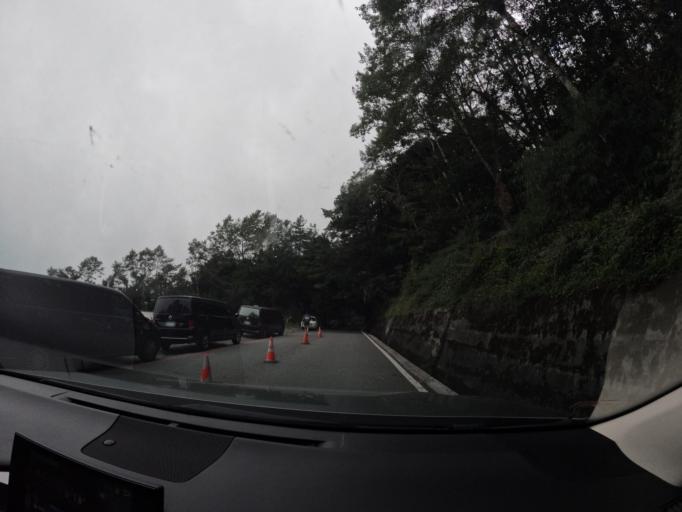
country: TW
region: Taiwan
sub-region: Taitung
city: Taitung
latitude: 23.2481
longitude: 120.9864
